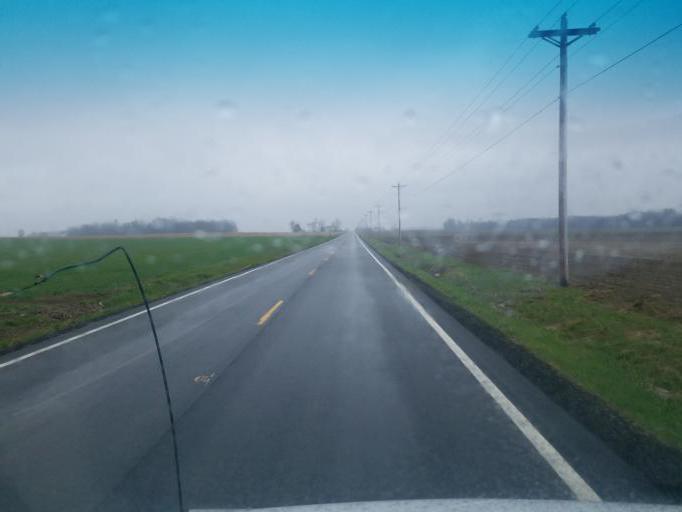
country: US
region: Ohio
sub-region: Crawford County
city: Bucyrus
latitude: 40.9651
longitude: -82.9135
